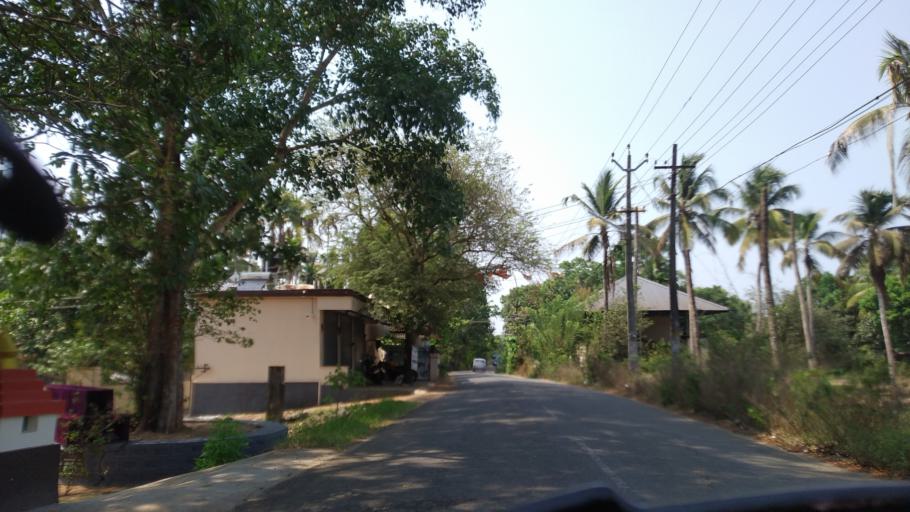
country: IN
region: Kerala
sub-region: Thrissur District
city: Kodungallur
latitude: 10.2595
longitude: 76.1452
